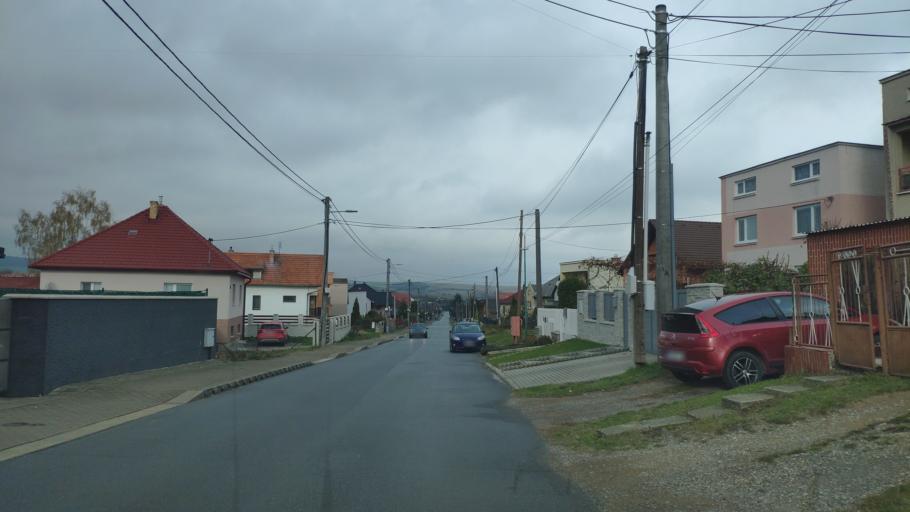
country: SK
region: Presovsky
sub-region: Okres Presov
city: Presov
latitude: 49.0047
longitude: 21.1879
